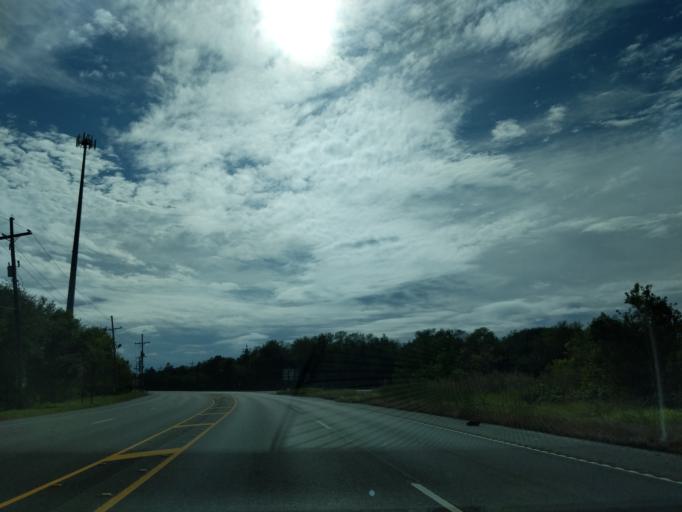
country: US
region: Louisiana
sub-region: Saint Tammany Parish
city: Eden Isle
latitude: 30.0753
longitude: -89.8608
